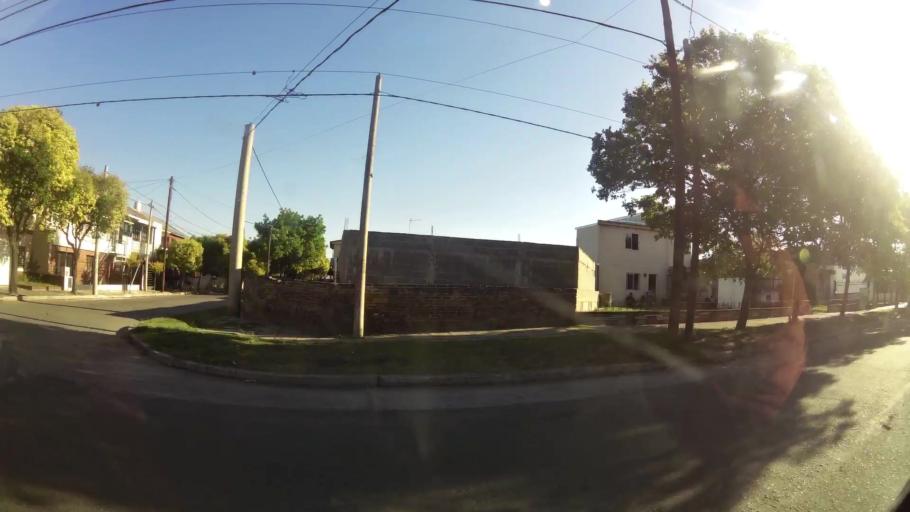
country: AR
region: Cordoba
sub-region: Departamento de Capital
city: Cordoba
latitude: -31.3766
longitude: -64.1772
